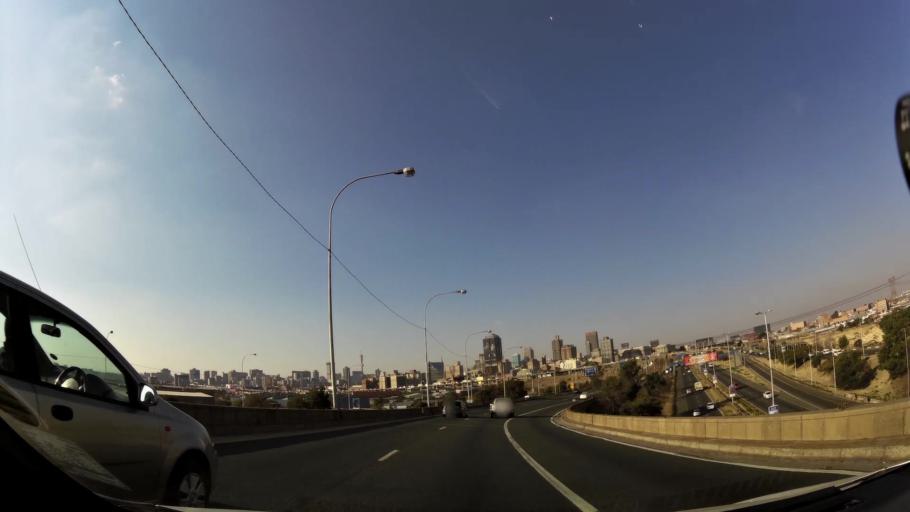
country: ZA
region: Gauteng
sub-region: City of Johannesburg Metropolitan Municipality
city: Johannesburg
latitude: -26.2115
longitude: 28.0253
